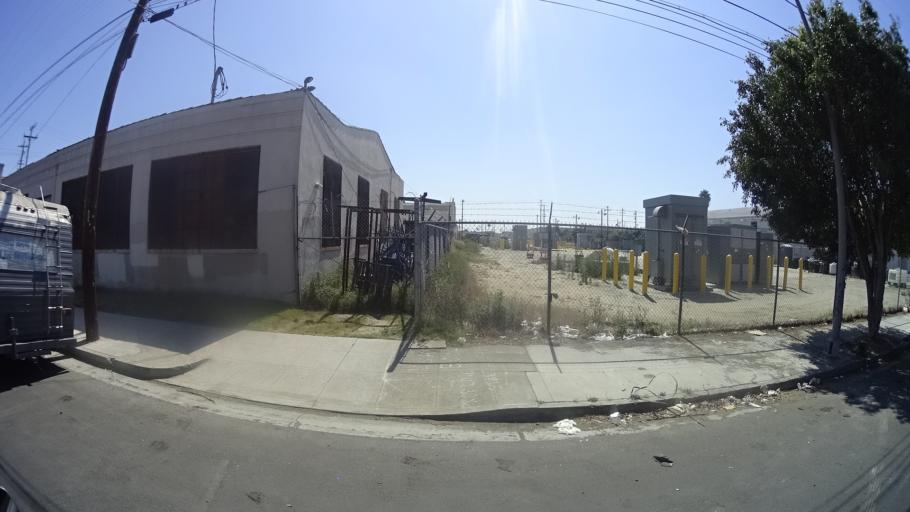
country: US
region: California
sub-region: Los Angeles County
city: View Park-Windsor Hills
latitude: 33.9829
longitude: -118.3135
